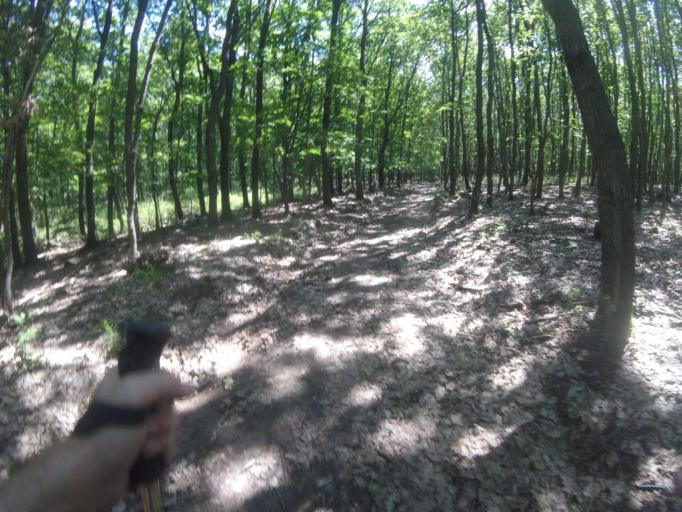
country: HU
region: Nograd
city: Matraverebely
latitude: 47.9309
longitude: 19.7975
